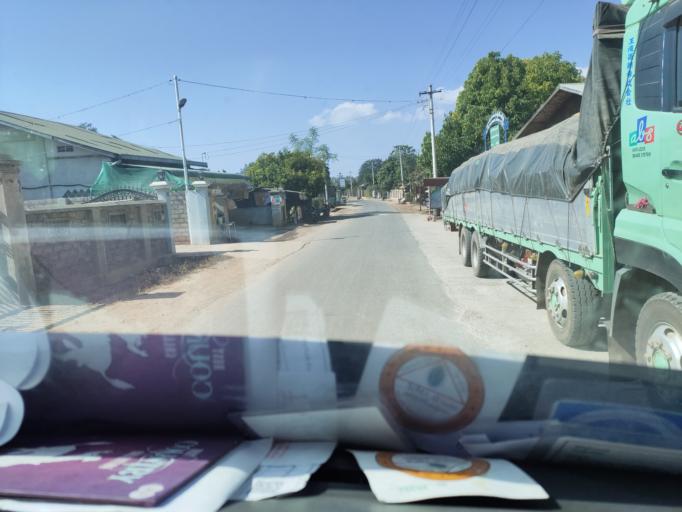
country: MM
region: Mandalay
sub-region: Pyin Oo Lwin District
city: Pyin Oo Lwin
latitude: 21.9531
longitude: 96.3943
